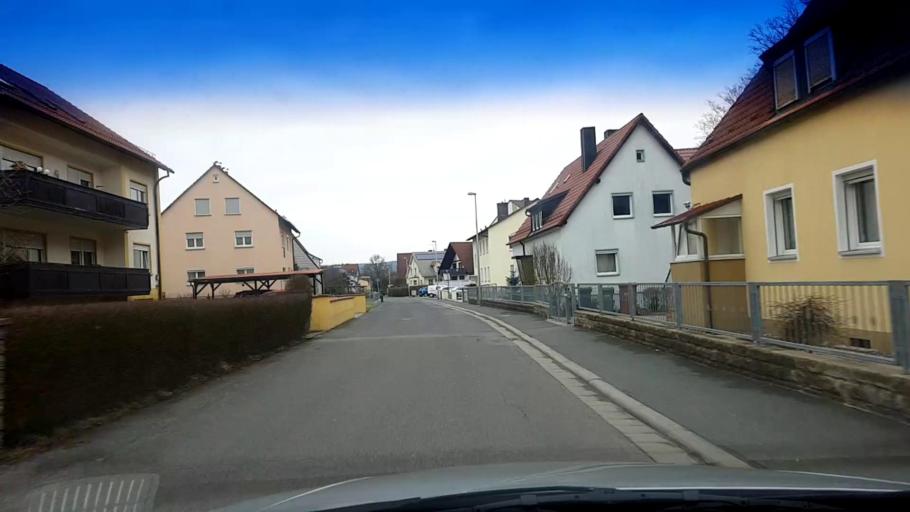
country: DE
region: Bavaria
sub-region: Upper Franconia
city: Bischberg
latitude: 49.9098
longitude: 10.8227
